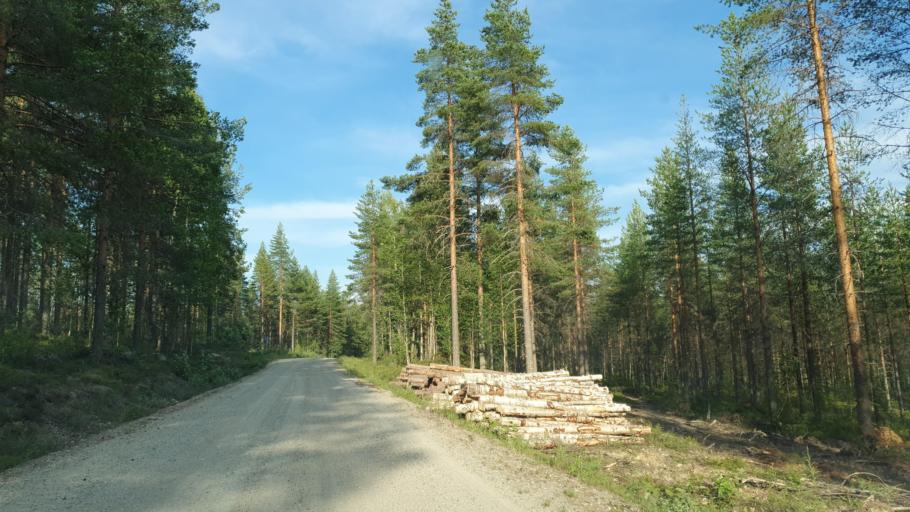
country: FI
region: Kainuu
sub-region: Kehys-Kainuu
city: Kuhmo
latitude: 64.2848
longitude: 29.7666
